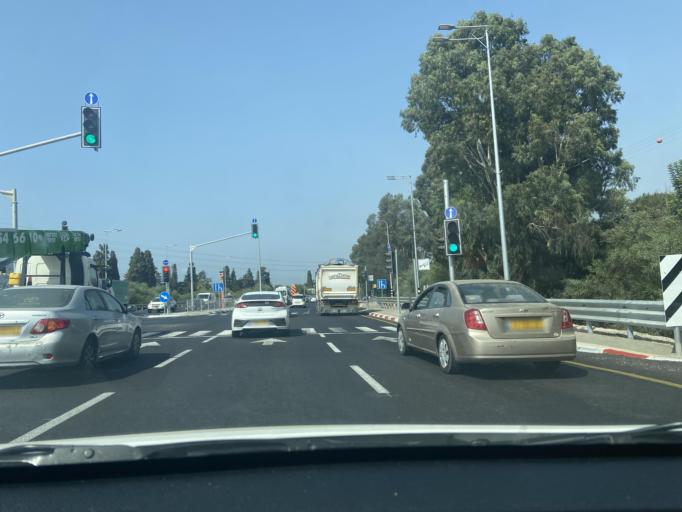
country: IL
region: Northern District
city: `Akko
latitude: 32.9516
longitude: 35.0909
